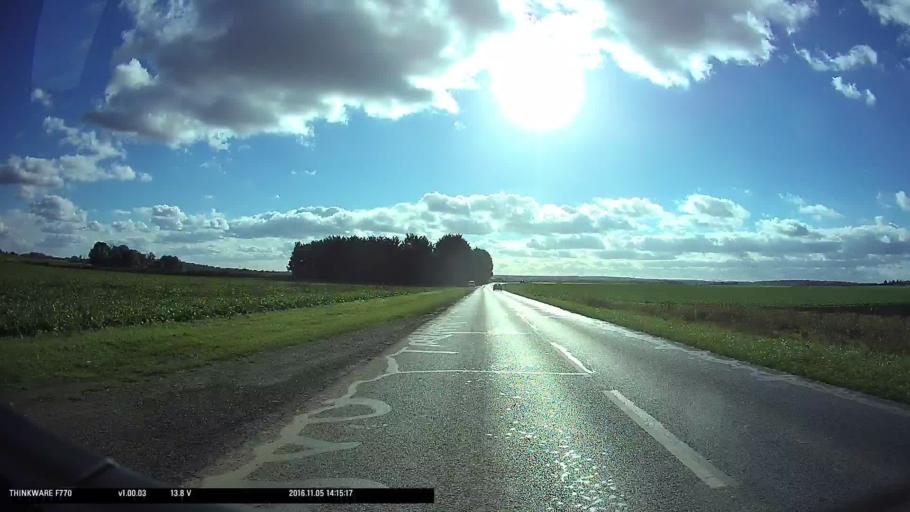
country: FR
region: Ile-de-France
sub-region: Departement du Val-d'Oise
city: Osny
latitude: 49.0875
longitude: 2.0572
